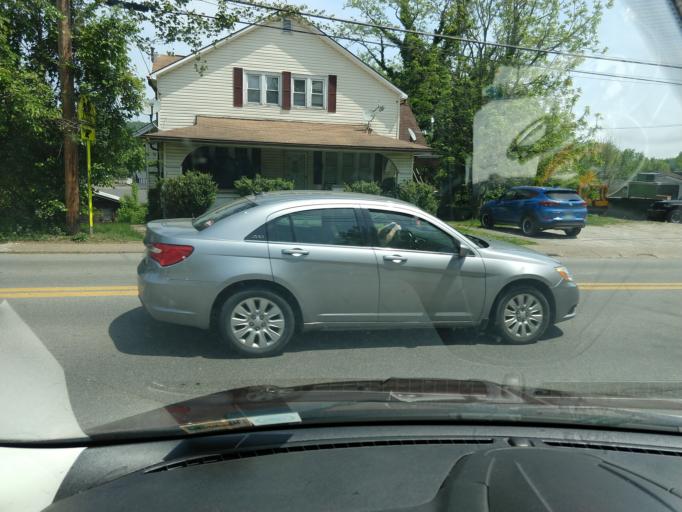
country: US
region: West Virginia
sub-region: Kanawha County
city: Saint Albans
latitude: 38.3831
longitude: -81.8306
